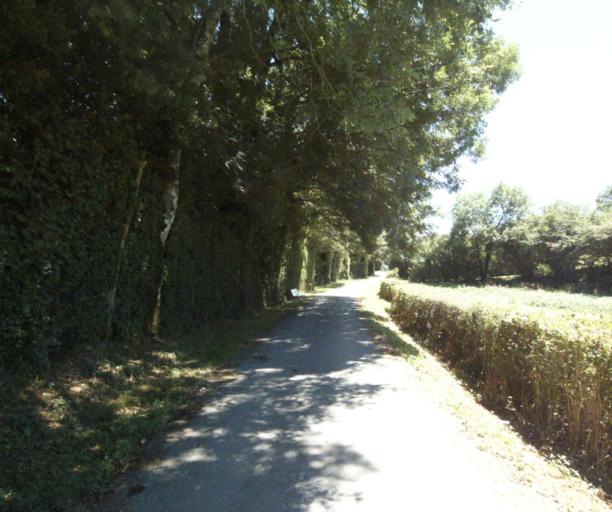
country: FR
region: Midi-Pyrenees
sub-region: Departement du Tarn
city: Dourgne
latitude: 43.4327
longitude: 2.1682
